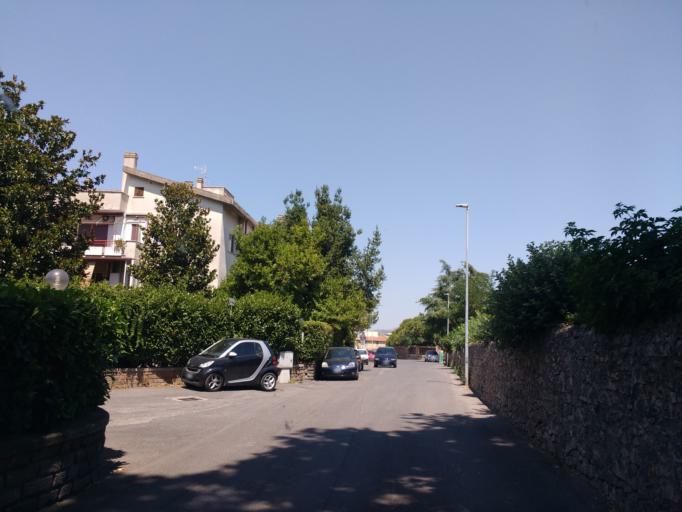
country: IT
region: Latium
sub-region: Citta metropolitana di Roma Capitale
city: Villa Adriana
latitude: 41.9515
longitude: 12.7782
